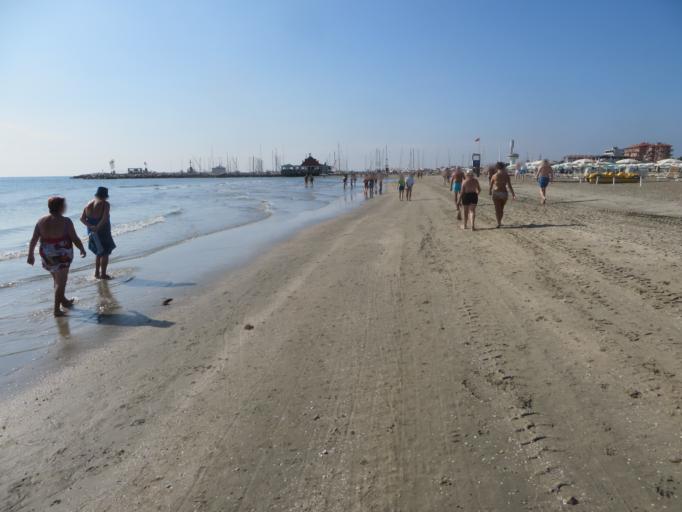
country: IT
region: Emilia-Romagna
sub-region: Provincia di Ravenna
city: Cervia
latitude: 44.2707
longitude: 12.3574
